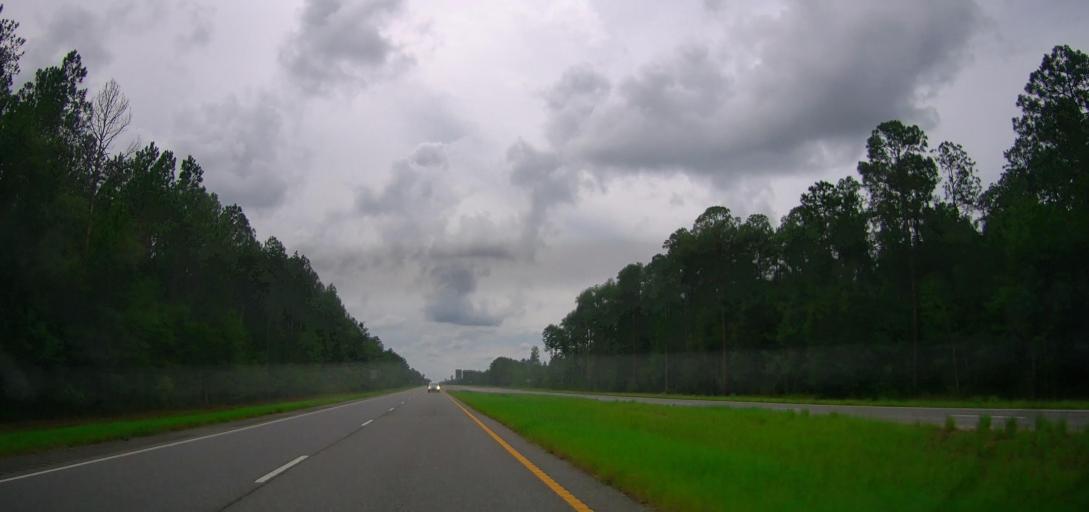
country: US
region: Georgia
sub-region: Wayne County
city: Jesup
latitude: 31.6701
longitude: -82.0549
